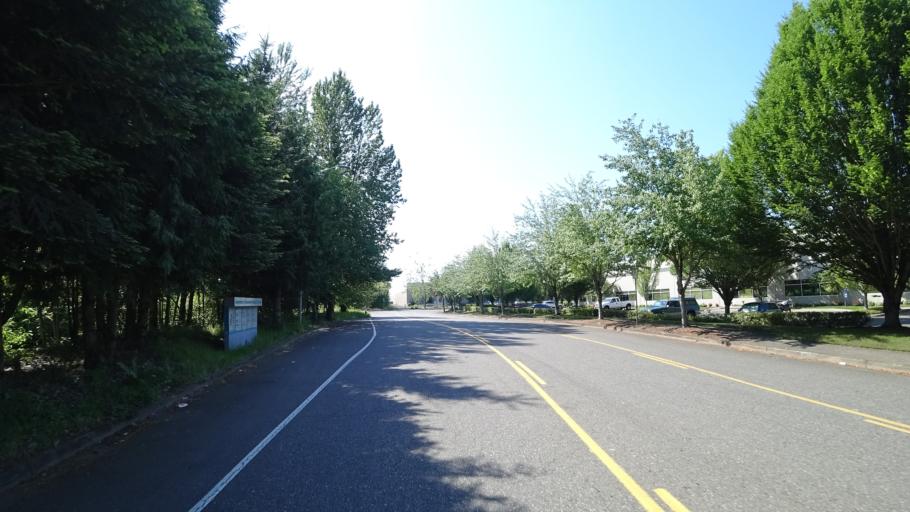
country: US
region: Oregon
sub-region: Multnomah County
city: Fairview
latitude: 45.5593
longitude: -122.4992
